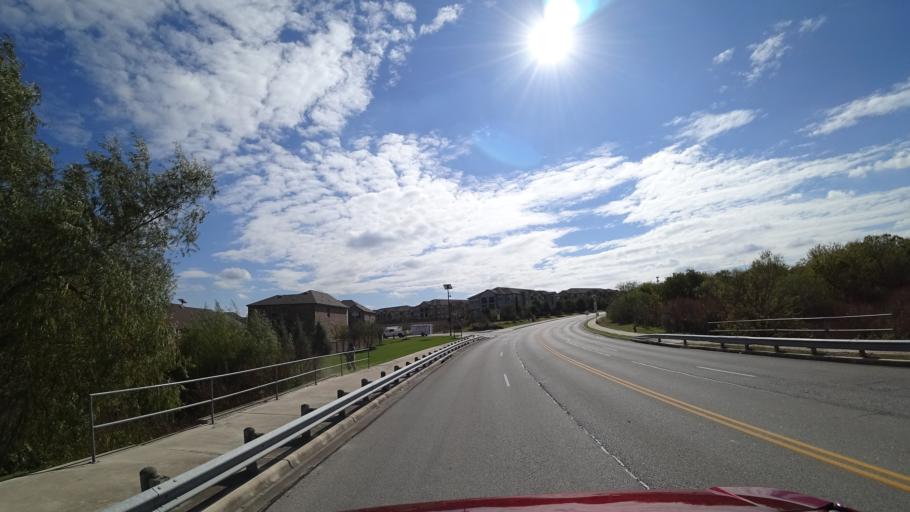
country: US
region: Texas
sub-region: Travis County
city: Pflugerville
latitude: 30.4509
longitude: -97.6298
